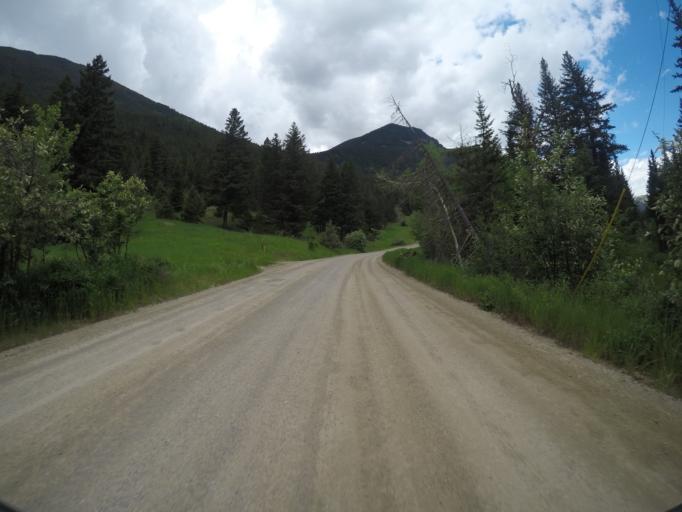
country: US
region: Montana
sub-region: Park County
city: Livingston
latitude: 45.4916
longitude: -110.2241
